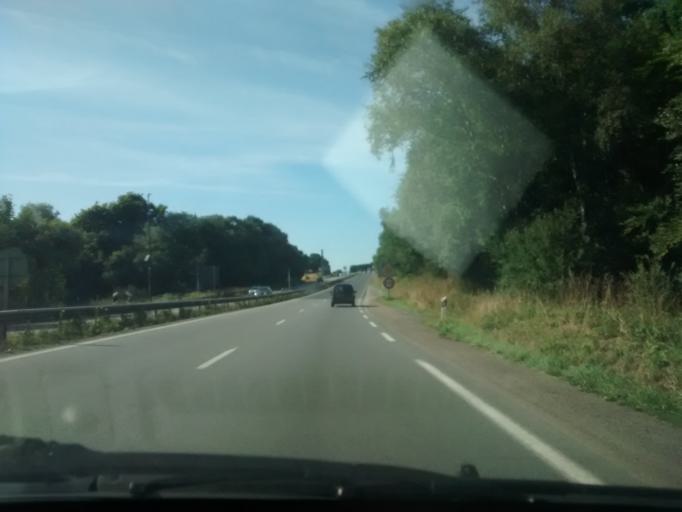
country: FR
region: Brittany
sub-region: Departement des Cotes-d'Armor
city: Graces
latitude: 48.5666
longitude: -3.2065
